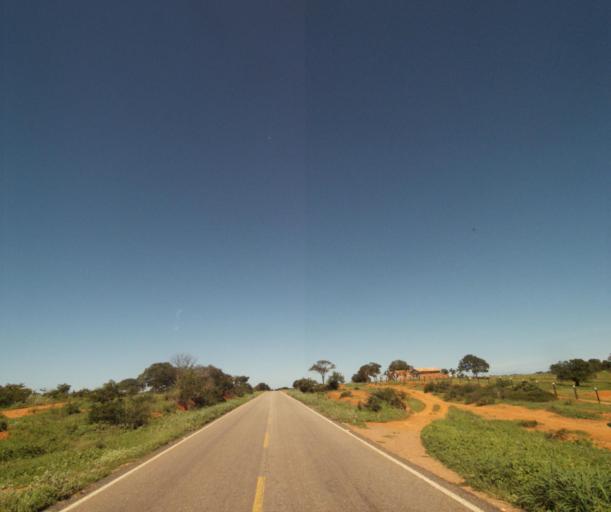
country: BR
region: Bahia
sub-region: Palmas De Monte Alto
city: Palmas de Monte Alto
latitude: -14.2592
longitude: -43.2816
